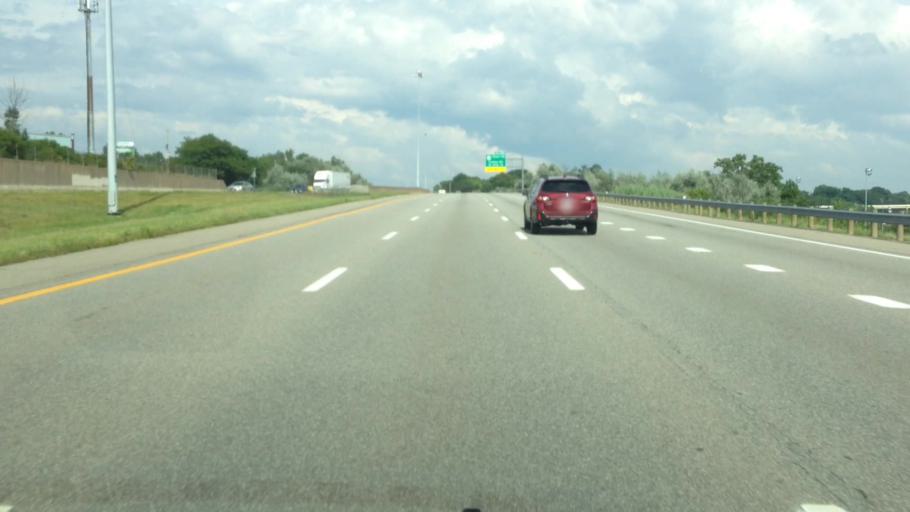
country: US
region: Ohio
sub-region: Cuyahoga County
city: Brooklyn
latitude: 41.4517
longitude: -81.7270
